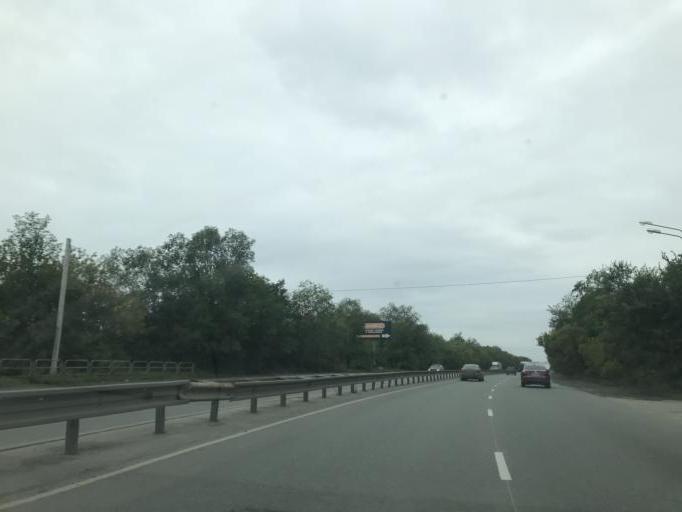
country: RU
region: Chelyabinsk
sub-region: Gorod Chelyabinsk
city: Chelyabinsk
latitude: 55.1748
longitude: 61.4234
